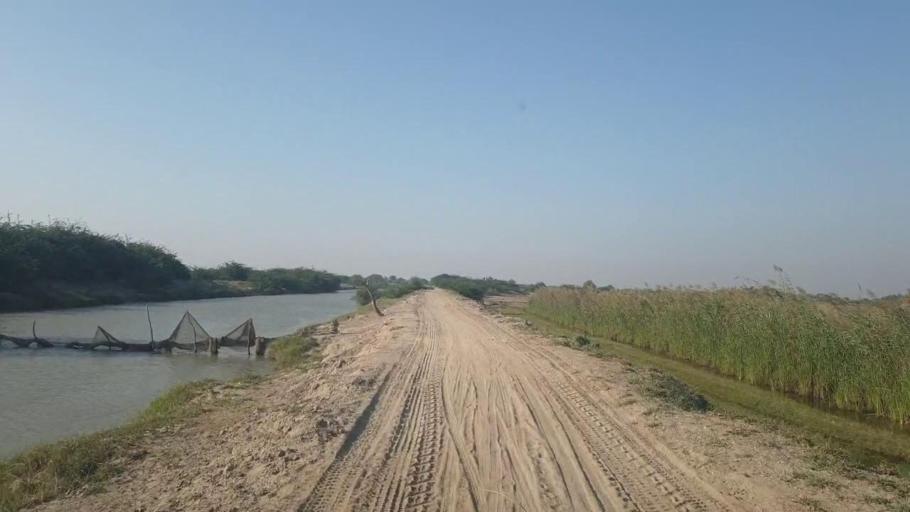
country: PK
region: Sindh
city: Tando Bago
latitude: 24.7241
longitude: 68.9217
